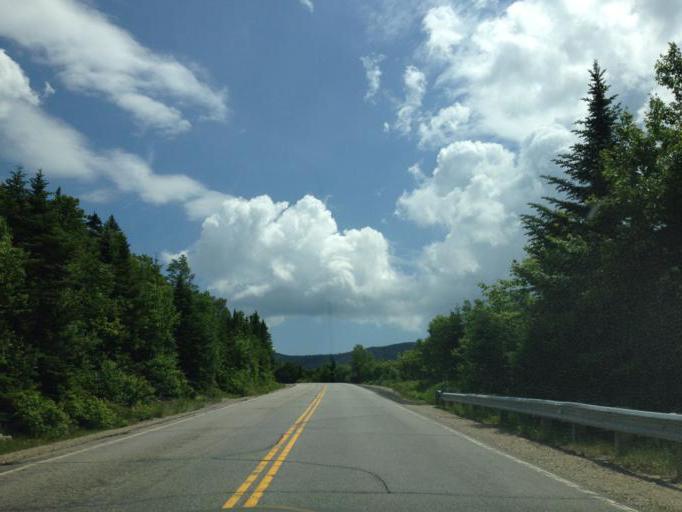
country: US
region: New Hampshire
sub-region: Grafton County
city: Woodstock
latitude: 44.0305
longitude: -71.4987
